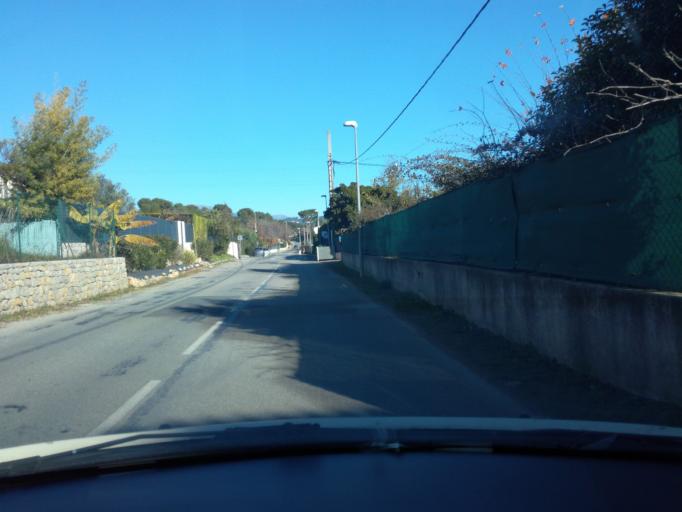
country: FR
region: Provence-Alpes-Cote d'Azur
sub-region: Departement des Alpes-Maritimes
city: La Roquette-sur-Siagne
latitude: 43.6032
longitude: 6.9534
